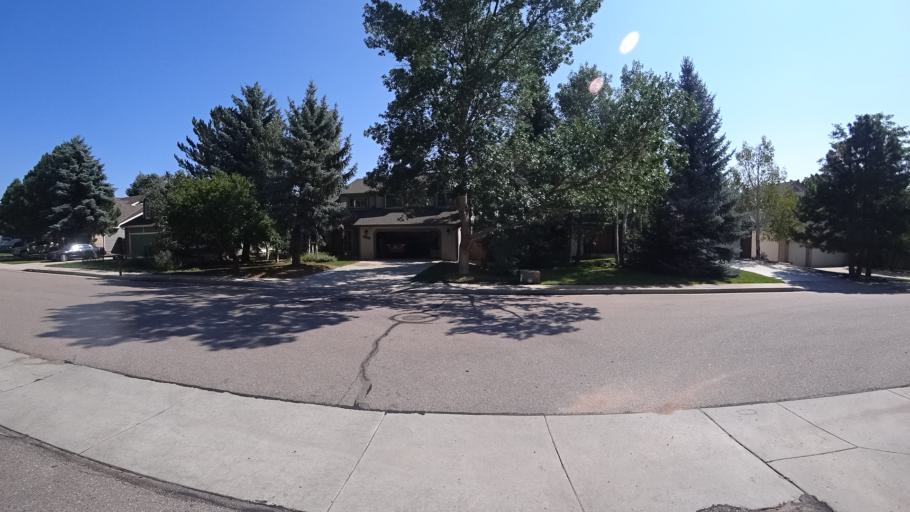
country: US
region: Colorado
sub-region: El Paso County
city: Air Force Academy
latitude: 38.9221
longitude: -104.8656
